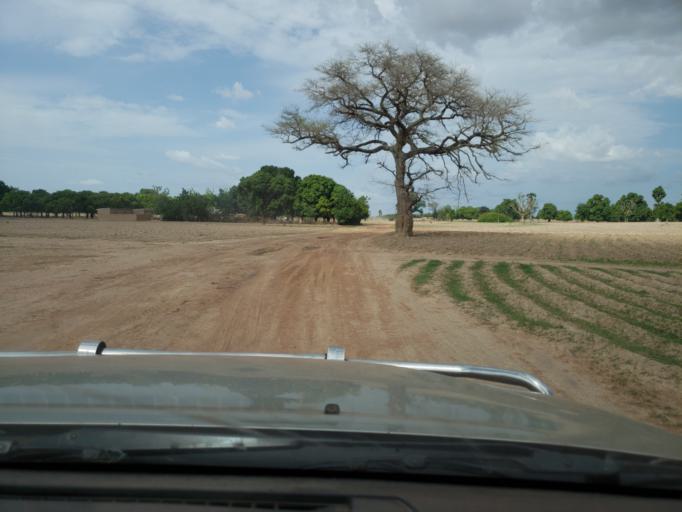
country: ML
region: Segou
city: Bla
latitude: 12.7351
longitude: -5.6621
